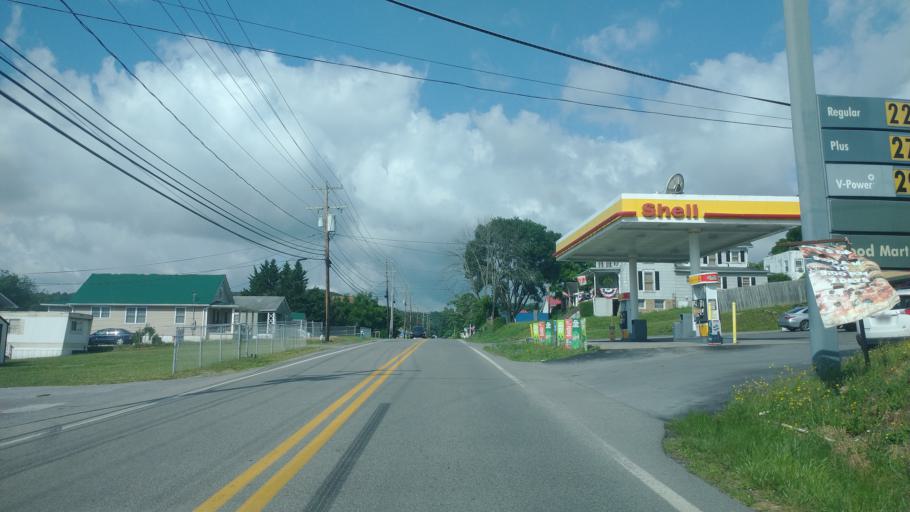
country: US
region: West Virginia
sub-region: Mercer County
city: Princeton
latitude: 37.3644
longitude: -81.1192
